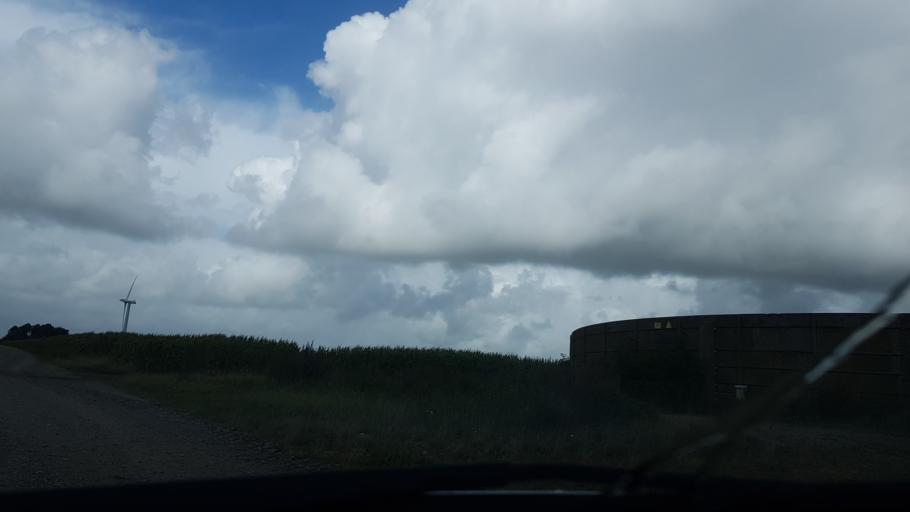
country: DK
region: South Denmark
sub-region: Esbjerg Kommune
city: Ribe
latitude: 55.2445
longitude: 8.7825
